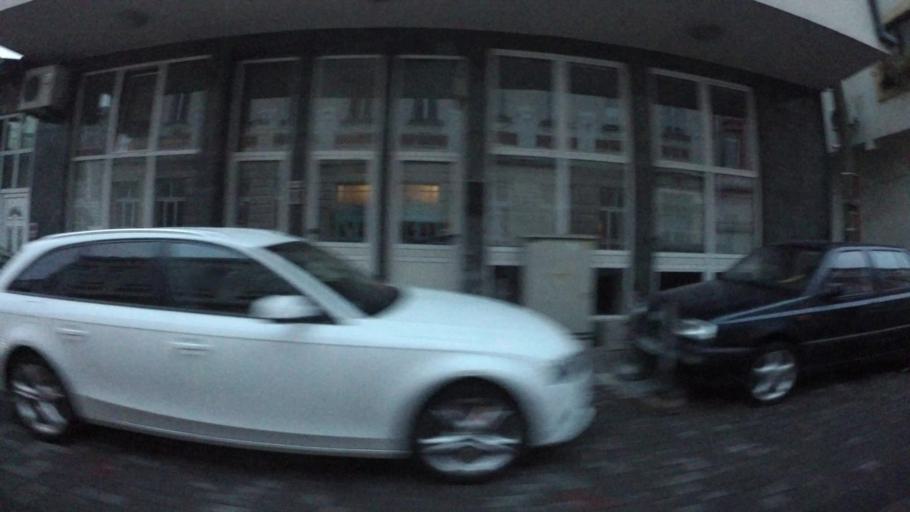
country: BA
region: Federation of Bosnia and Herzegovina
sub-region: Hercegovacko-Bosanski Kanton
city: Mostar
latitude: 43.3345
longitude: 17.8173
